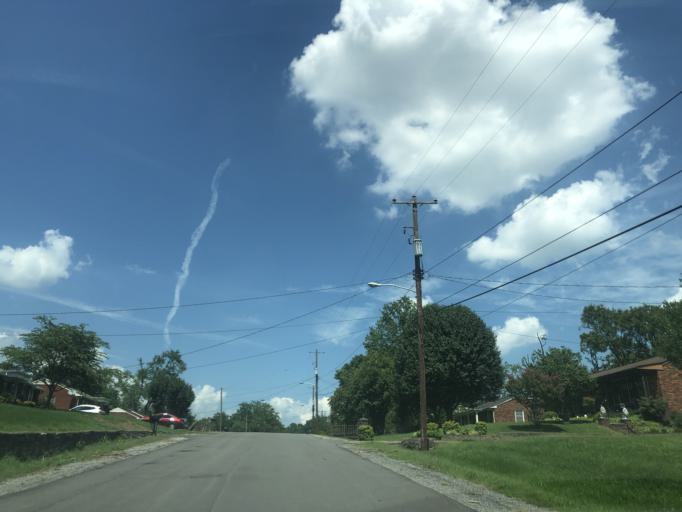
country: US
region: Tennessee
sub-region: Davidson County
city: Lakewood
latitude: 36.1790
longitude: -86.6479
